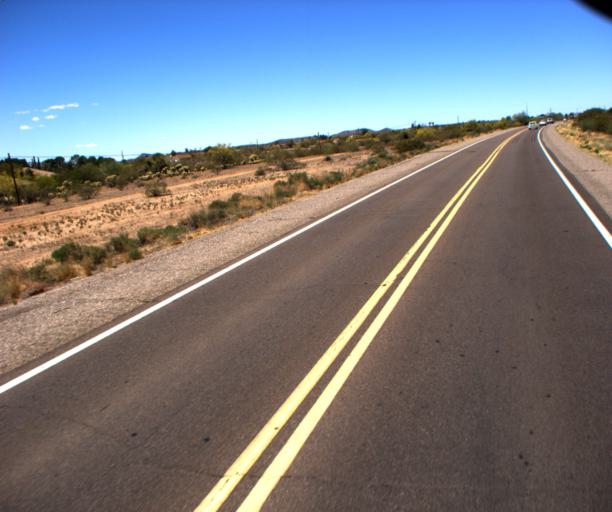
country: US
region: Arizona
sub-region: Maricopa County
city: Wickenburg
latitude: 34.0002
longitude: -112.7647
